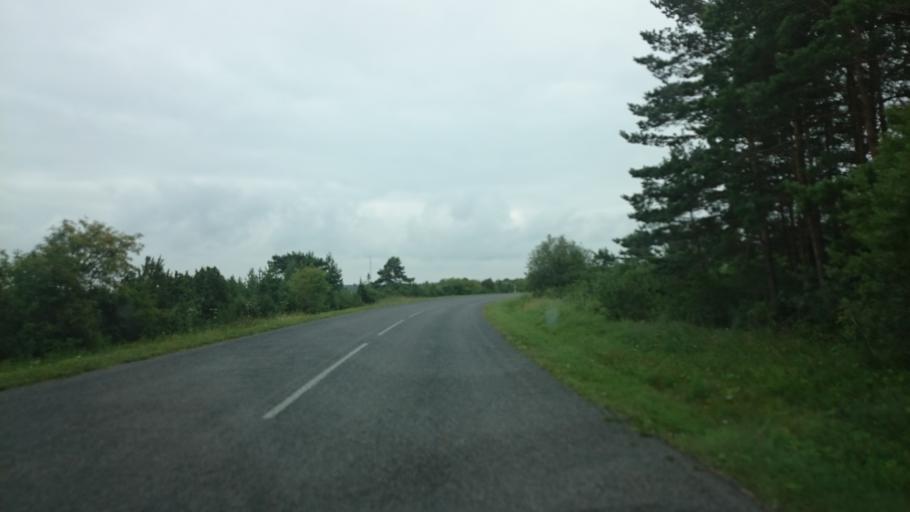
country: EE
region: Saare
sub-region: Orissaare vald
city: Orissaare
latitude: 58.5851
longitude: 23.0250
